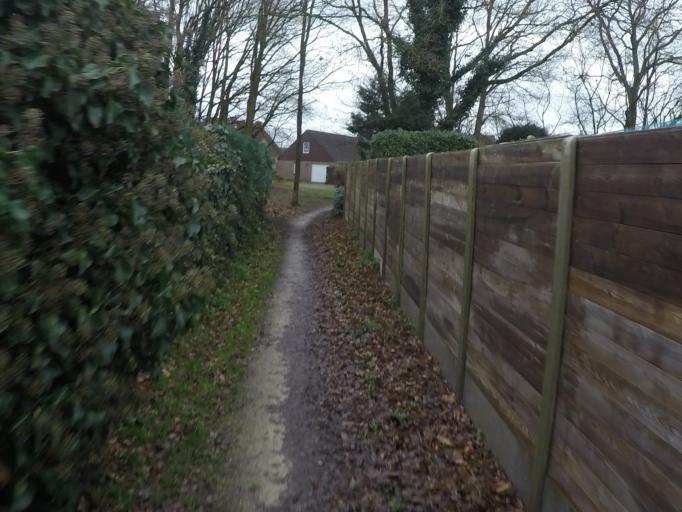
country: BE
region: Flanders
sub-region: Provincie Antwerpen
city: Schilde
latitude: 51.2163
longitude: 4.5889
